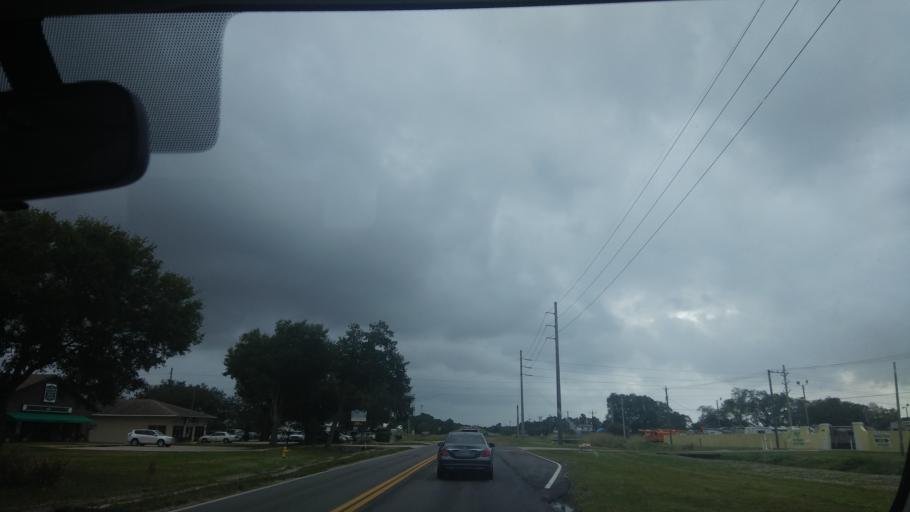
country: US
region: Florida
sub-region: Brevard County
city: Palm Bay
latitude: 27.9932
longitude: -80.6220
